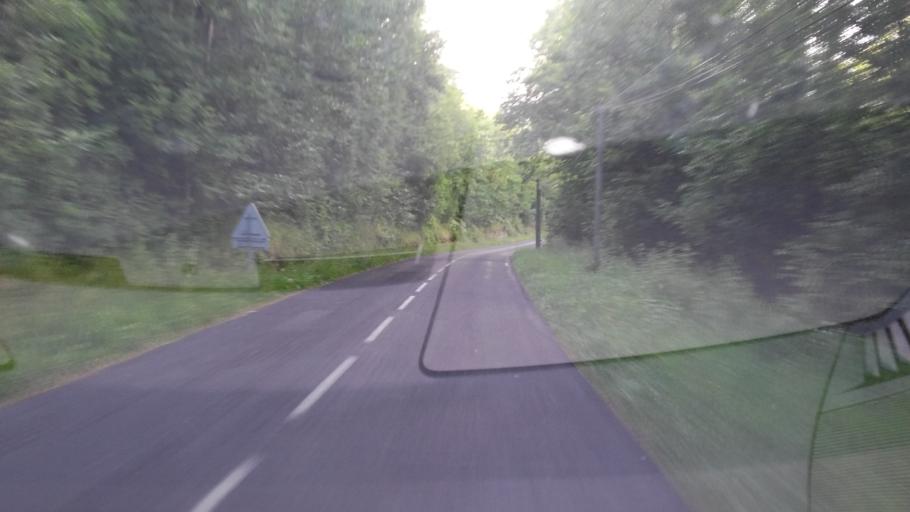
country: FR
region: Languedoc-Roussillon
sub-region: Departement de la Lozere
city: Meyrueis
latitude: 44.0165
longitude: 3.3635
